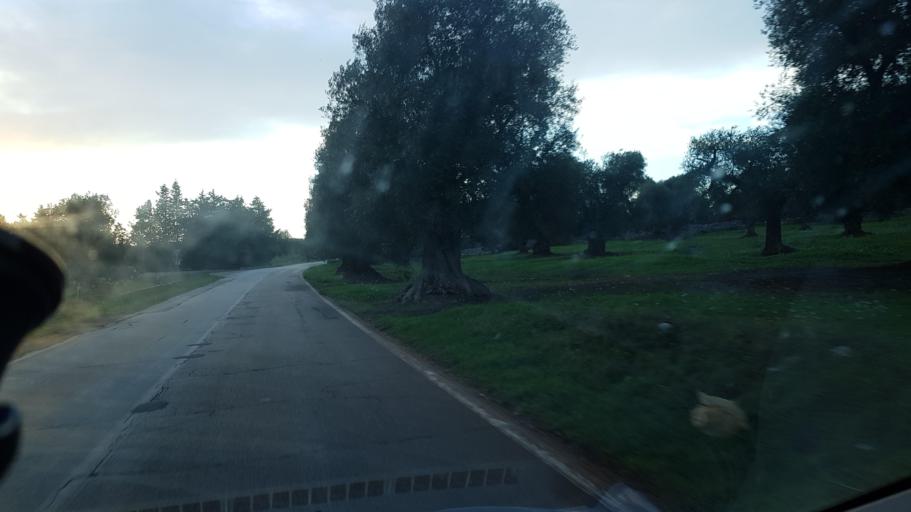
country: IT
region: Apulia
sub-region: Provincia di Brindisi
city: Ceglie Messapica
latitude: 40.6436
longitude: 17.5417
